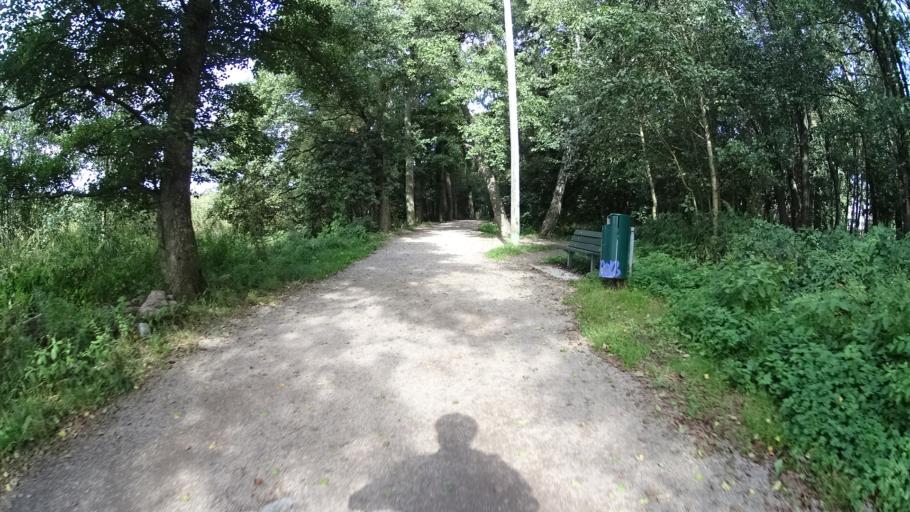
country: FI
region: Uusimaa
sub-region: Helsinki
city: Teekkarikylae
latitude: 60.1529
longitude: 24.8749
